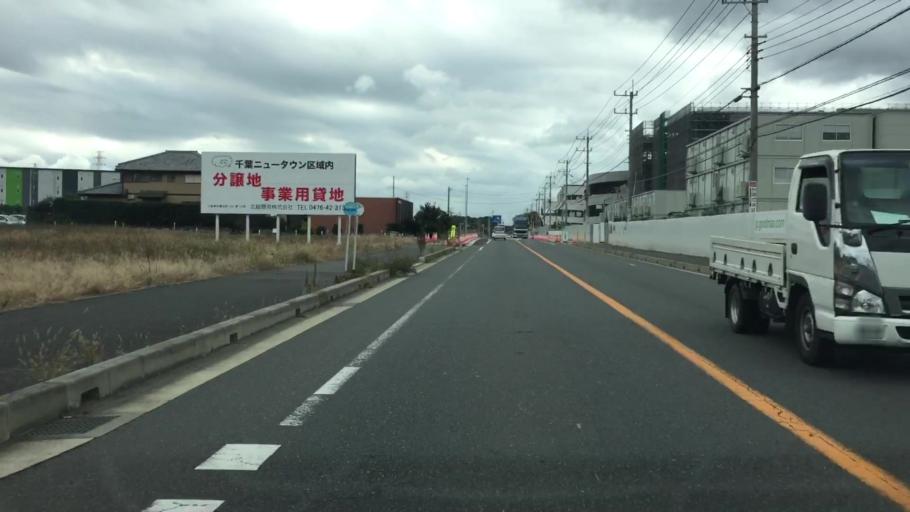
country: JP
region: Chiba
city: Shiroi
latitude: 35.8180
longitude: 140.1355
